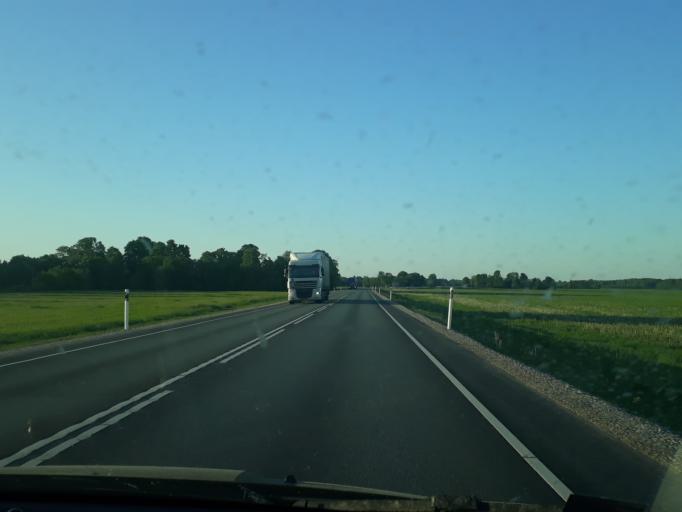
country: EE
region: Paernumaa
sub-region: Tootsi vald
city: Tootsi
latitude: 58.5464
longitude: 24.8469
